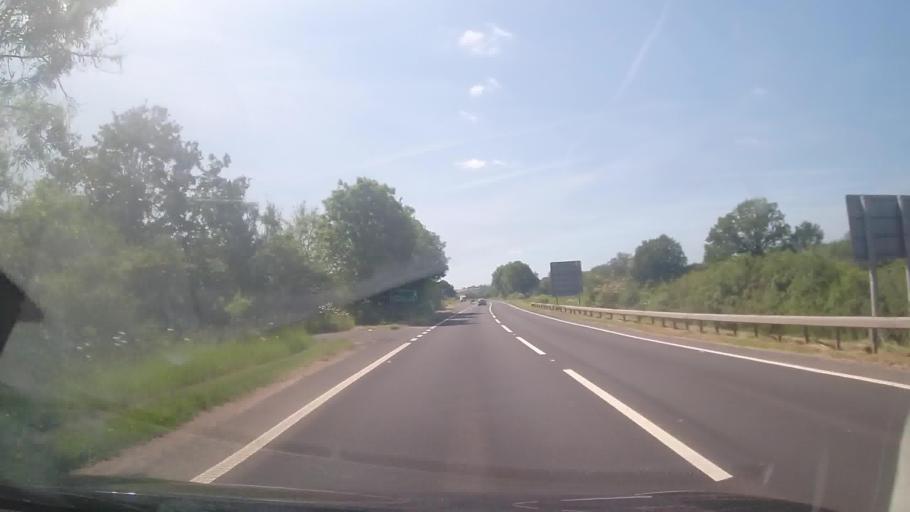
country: GB
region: England
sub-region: Herefordshire
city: Leominster
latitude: 52.2197
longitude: -2.7258
